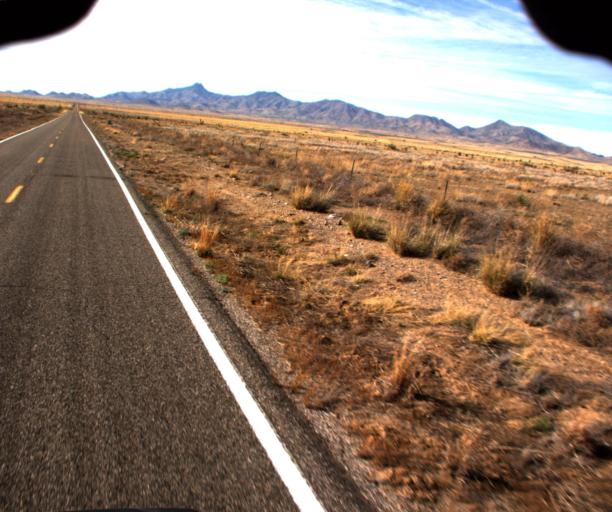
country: US
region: Arizona
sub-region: Cochise County
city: Willcox
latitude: 32.0637
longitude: -109.5045
